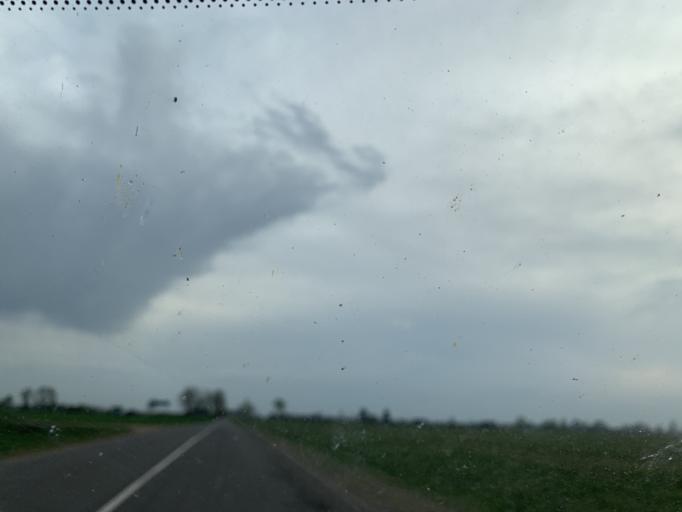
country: BY
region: Minsk
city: Kapyl'
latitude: 53.2981
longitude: 27.0387
